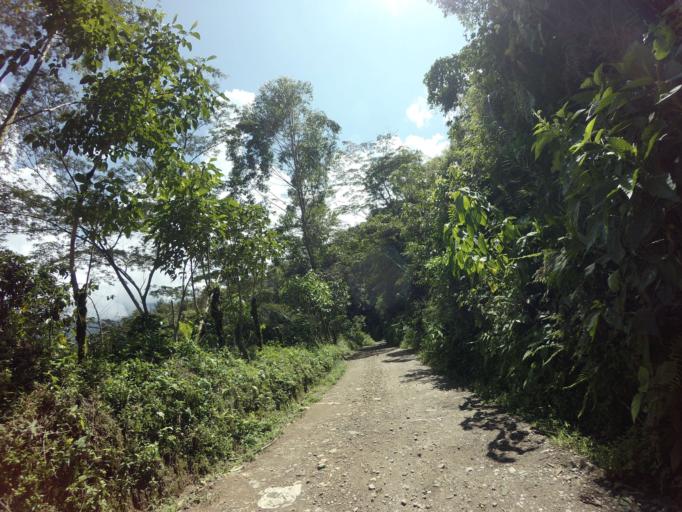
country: CO
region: Caldas
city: Pensilvania
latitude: 5.4854
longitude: -75.1779
